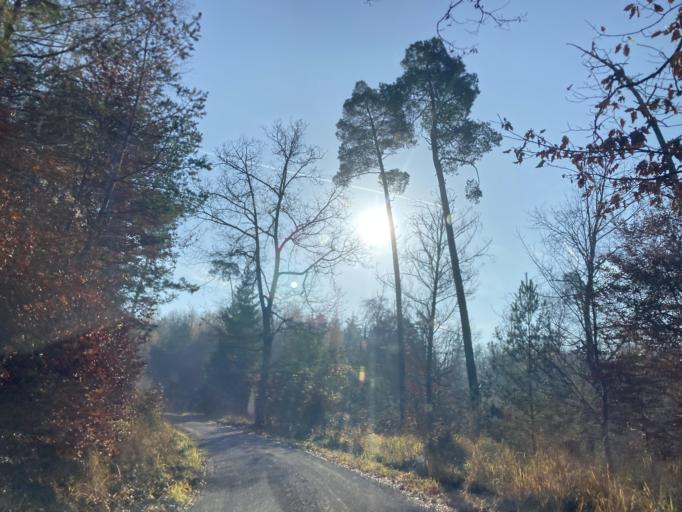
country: DE
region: Baden-Wuerttemberg
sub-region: Regierungsbezirk Stuttgart
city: Hildrizhausen
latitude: 48.5769
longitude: 8.9806
